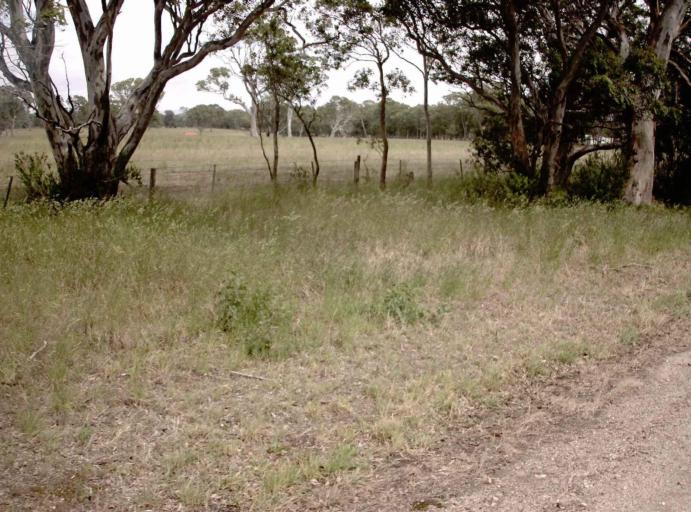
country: AU
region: Victoria
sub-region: Wellington
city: Sale
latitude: -37.9218
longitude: 147.0867
